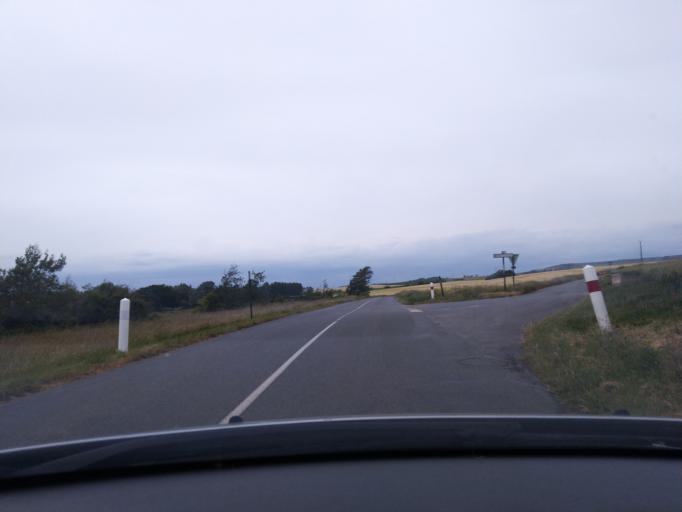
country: FR
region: Nord-Pas-de-Calais
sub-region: Departement du Pas-de-Calais
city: Marquise
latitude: 50.8349
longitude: 1.6863
